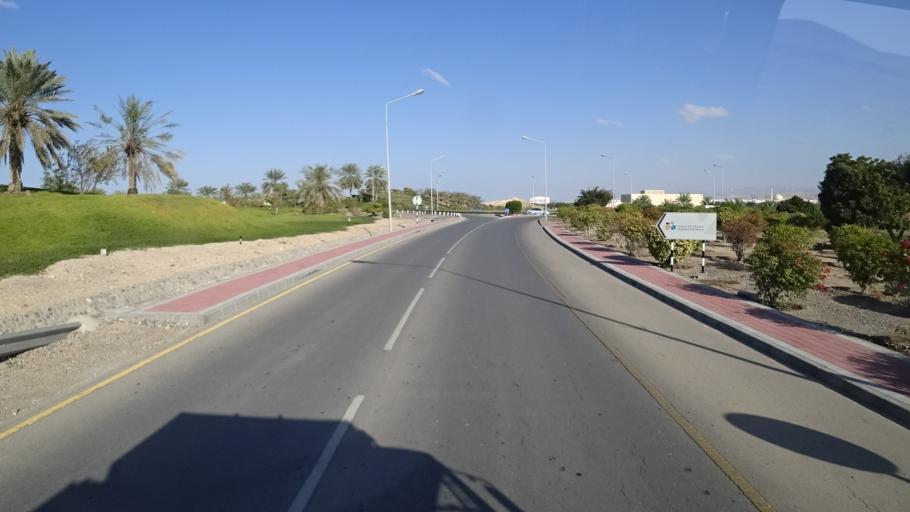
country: OM
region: Muhafazat Masqat
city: As Sib al Jadidah
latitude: 23.5871
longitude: 58.1759
